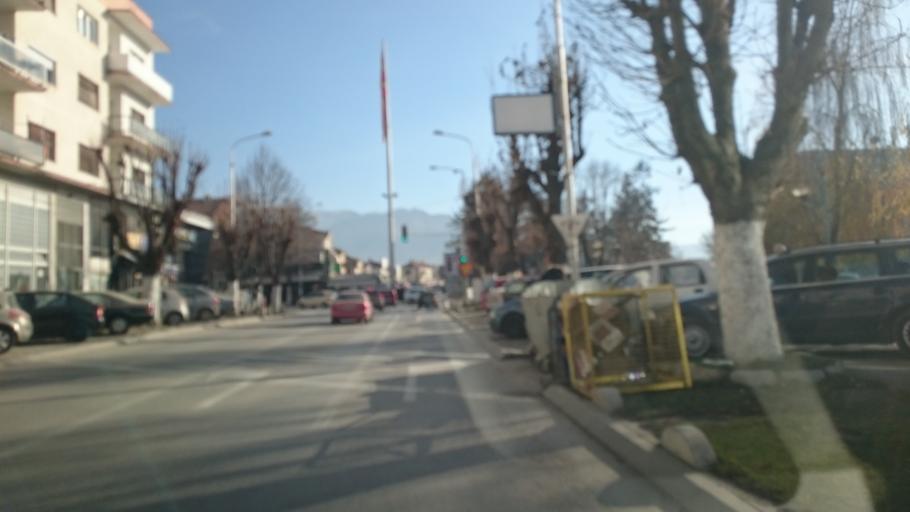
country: MK
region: Prilep
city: Prilep
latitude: 41.3467
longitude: 21.5532
